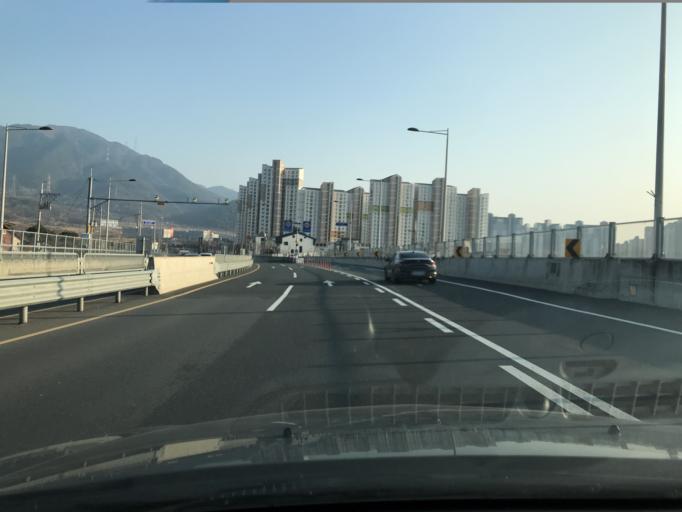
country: KR
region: Daegu
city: Hwawon
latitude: 35.7038
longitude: 128.4659
